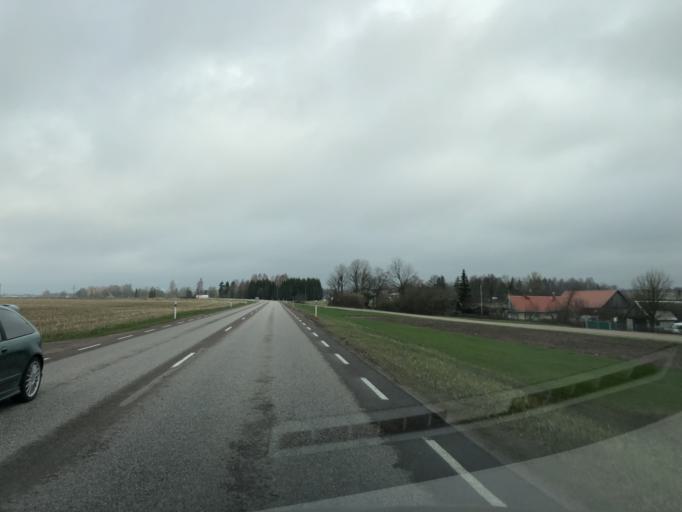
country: EE
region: Jogevamaa
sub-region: Jogeva linn
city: Jogeva
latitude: 58.7190
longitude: 26.3962
